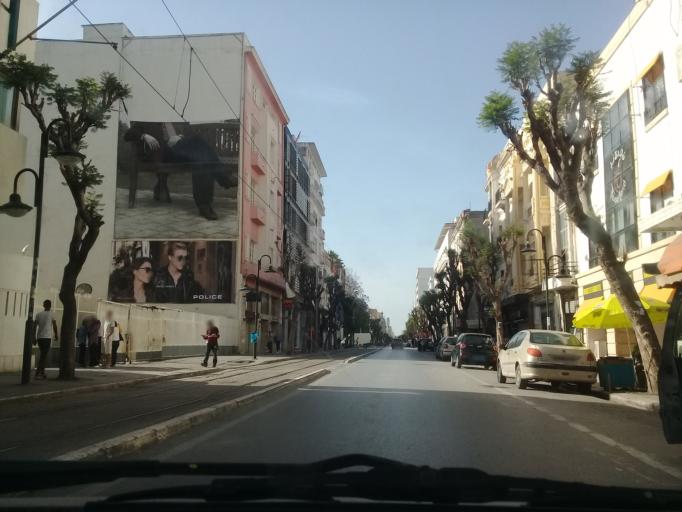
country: TN
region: Tunis
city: Tunis
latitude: 36.8002
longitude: 10.1813
